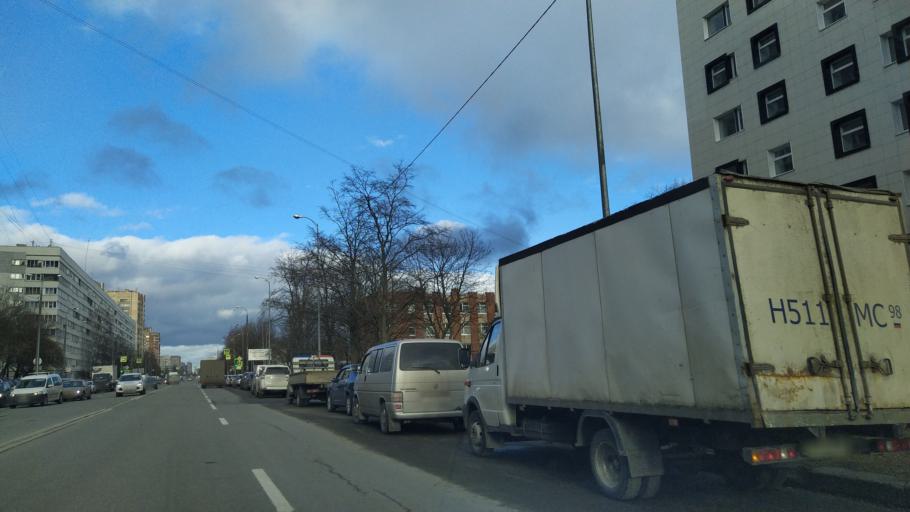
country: RU
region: St.-Petersburg
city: Grazhdanka
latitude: 60.0353
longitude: 30.3808
